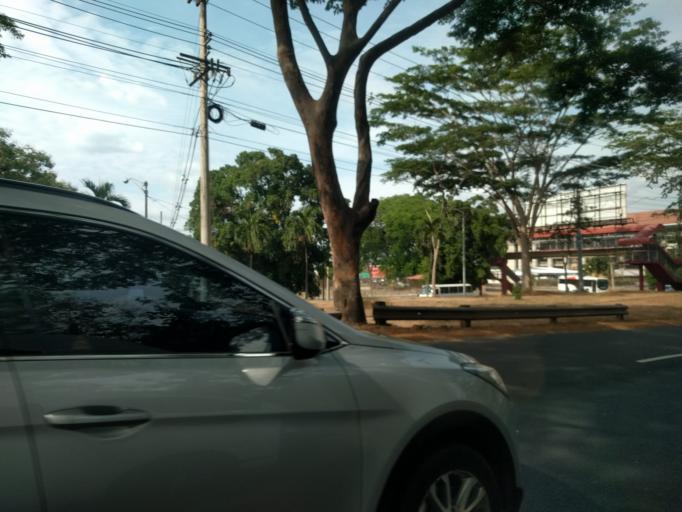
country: PA
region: Panama
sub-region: Distrito de Panama
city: Ancon
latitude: 8.9657
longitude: -79.5508
